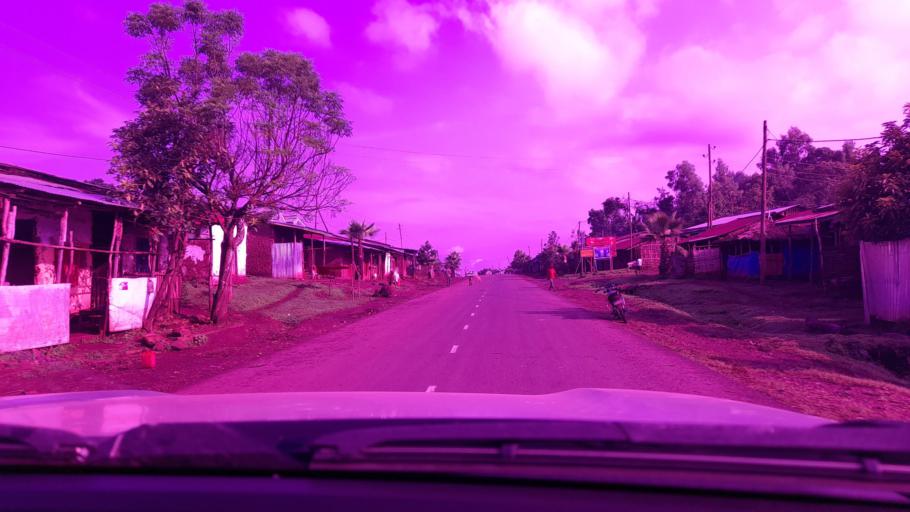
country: ET
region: Oromiya
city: Bedele
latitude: 8.1738
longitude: 36.4595
